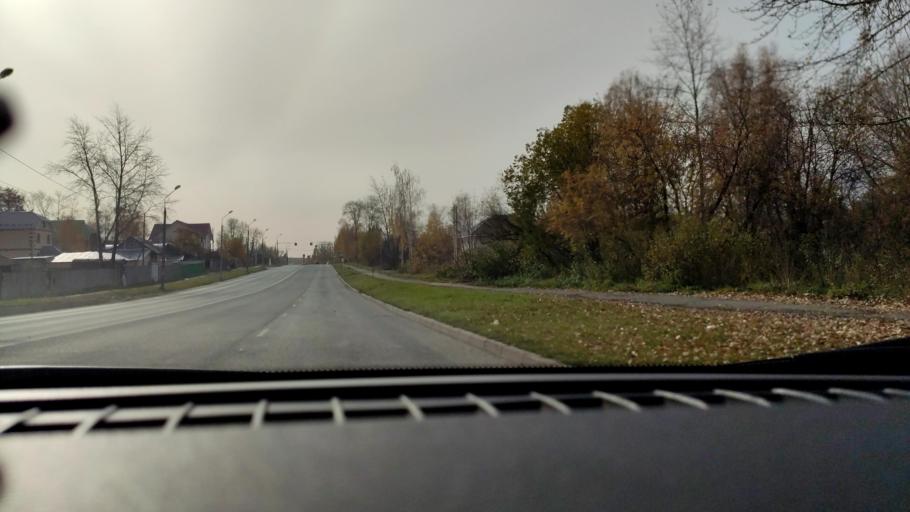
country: RU
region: Perm
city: Polazna
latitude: 58.1257
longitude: 56.4054
